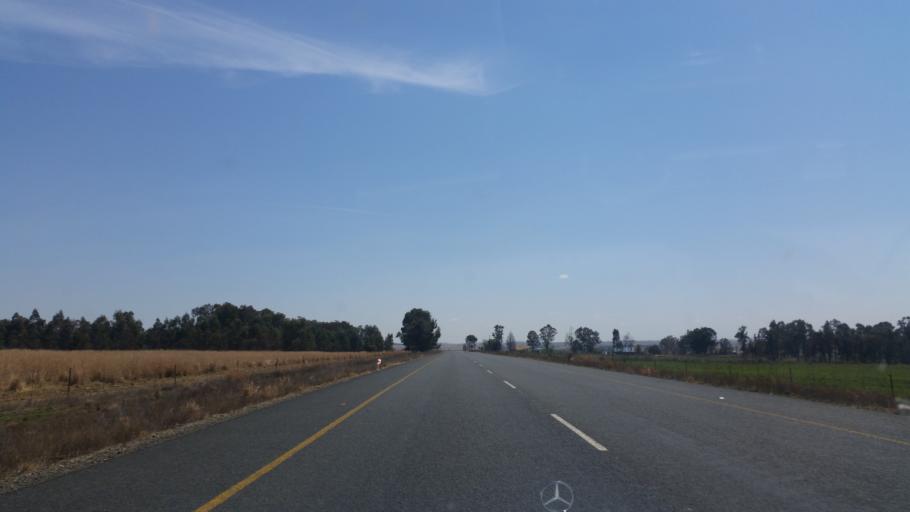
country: ZA
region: Orange Free State
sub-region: Thabo Mofutsanyana District Municipality
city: Phuthaditjhaba
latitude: -28.2149
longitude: 28.6955
